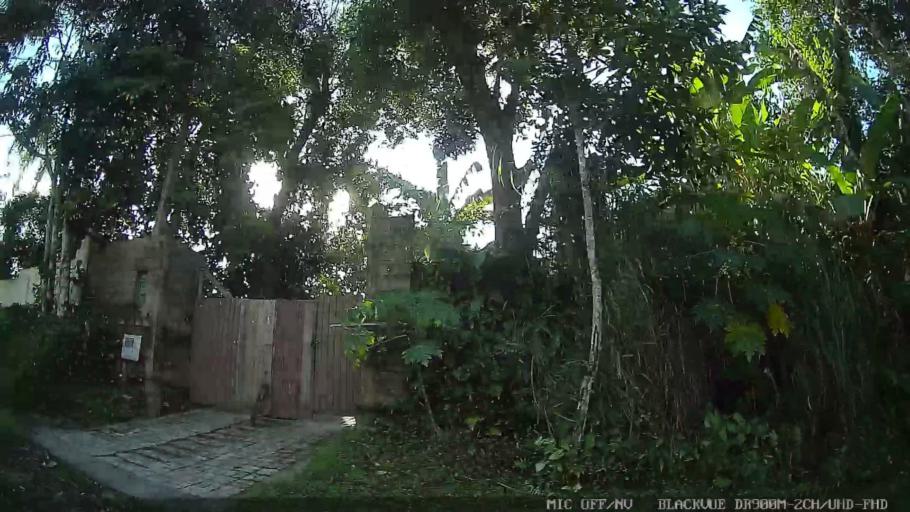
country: BR
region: Sao Paulo
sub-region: Itanhaem
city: Itanhaem
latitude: -24.1754
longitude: -46.8248
